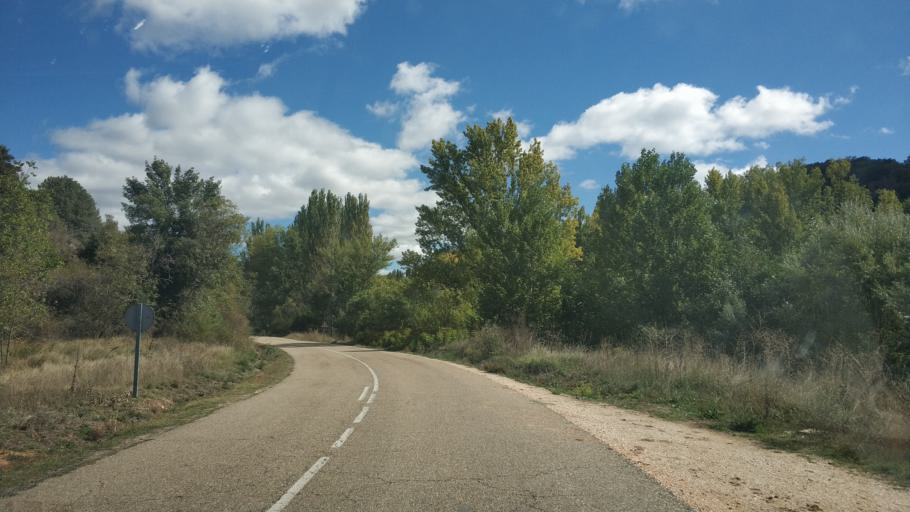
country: ES
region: Castille and Leon
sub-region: Provincia de Burgos
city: Covarrubias
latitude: 42.0542
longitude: -3.5086
